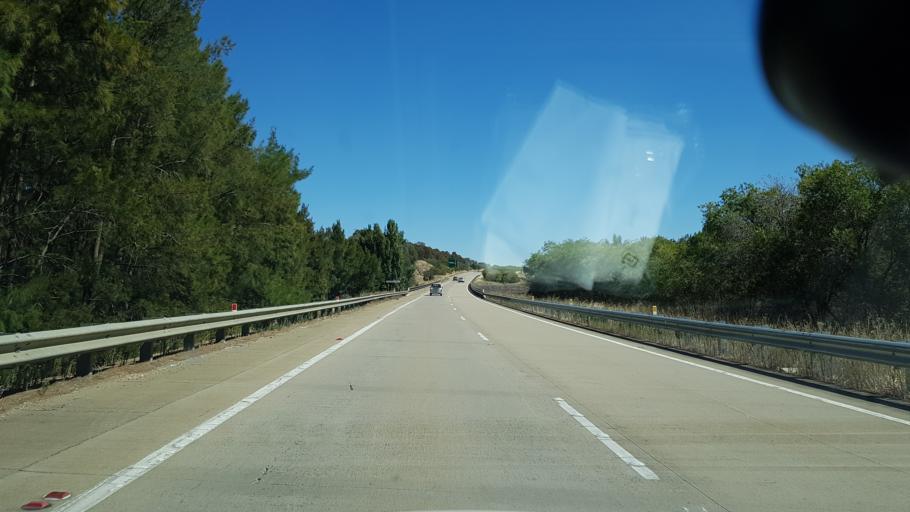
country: AU
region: New South Wales
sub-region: Gundagai
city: Gundagai
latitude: -34.8198
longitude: 148.3752
